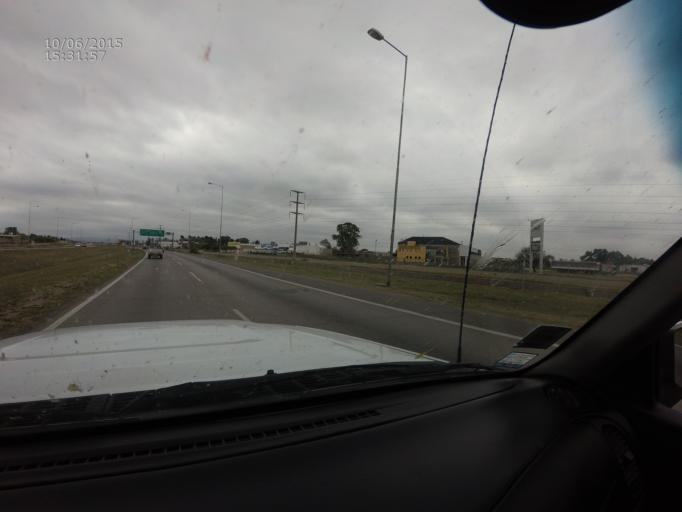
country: AR
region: Cordoba
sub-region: Departamento de Capital
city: Cordoba
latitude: -31.3642
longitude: -64.1354
